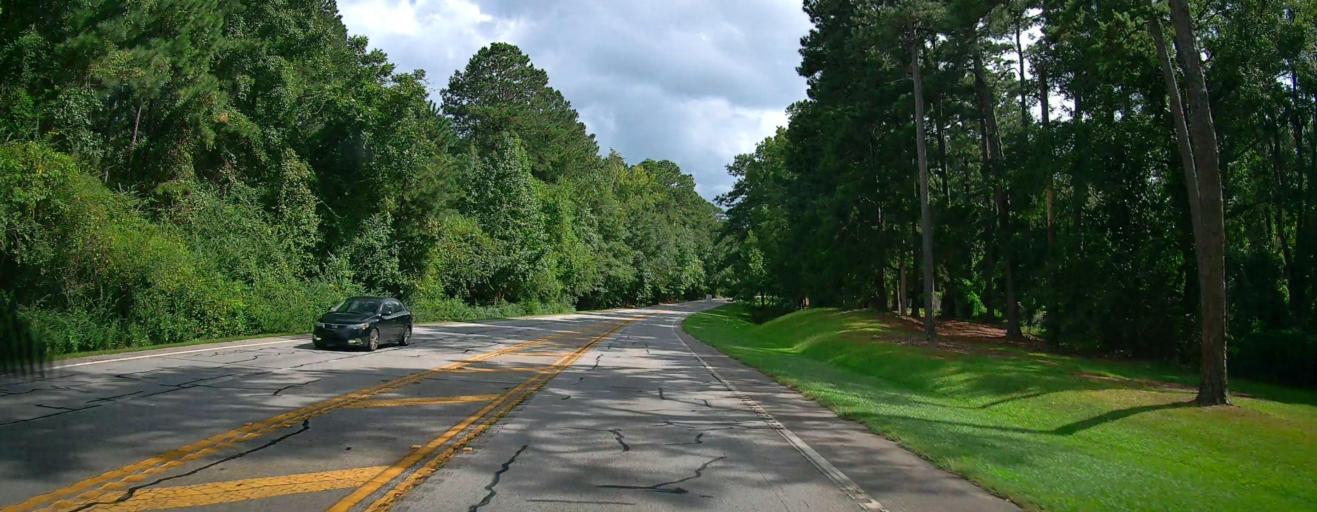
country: US
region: Georgia
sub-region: Harris County
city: Pine Mountain
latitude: 32.8448
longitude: -84.8438
